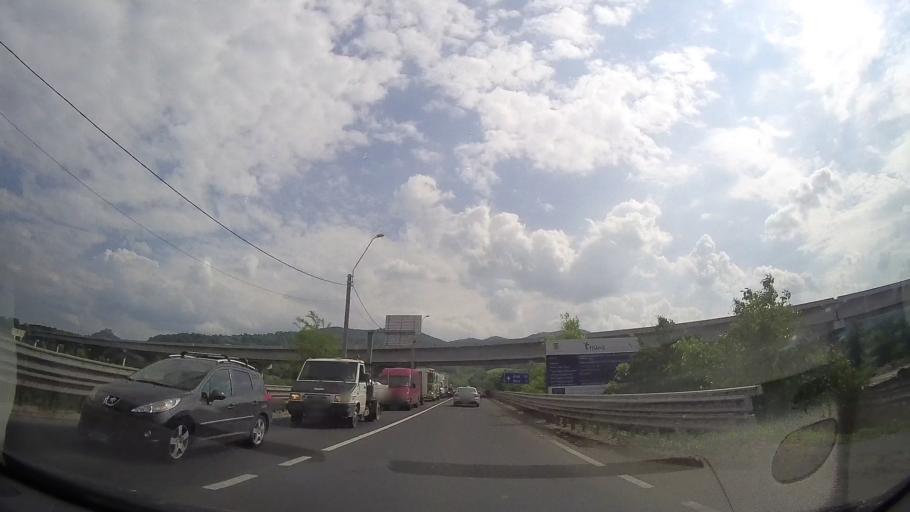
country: RO
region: Hunedoara
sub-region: Comuna Soimus
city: Soimus
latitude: 45.9135
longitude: 22.8770
